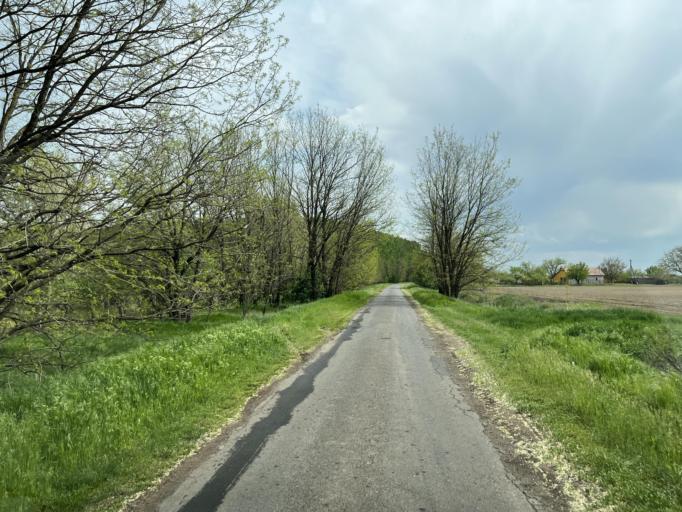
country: HU
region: Pest
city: Nagykoros
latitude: 46.9774
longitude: 19.8123
